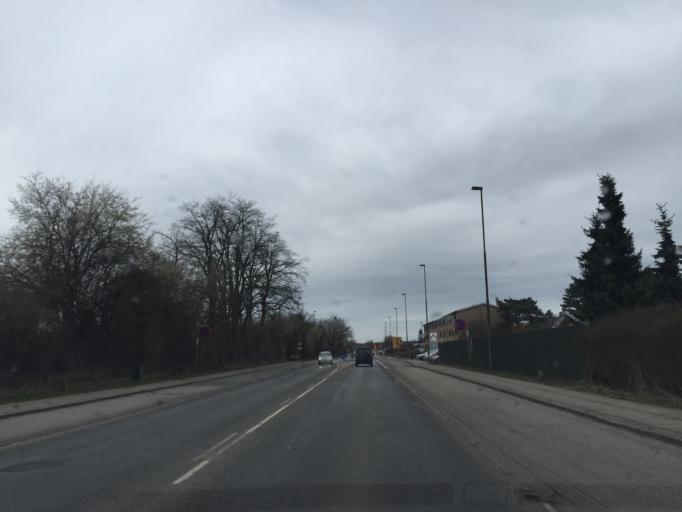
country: DK
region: South Denmark
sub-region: Odense Kommune
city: Odense
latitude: 55.4037
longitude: 10.3401
